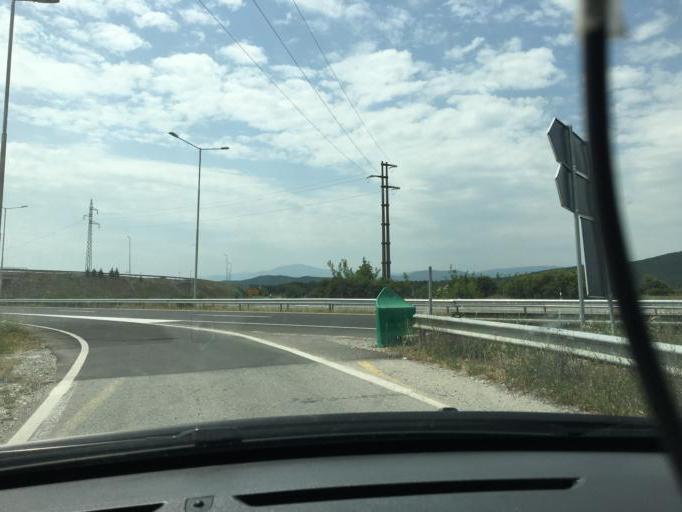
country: MK
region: Gevgelija
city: Gevgelija
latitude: 41.2050
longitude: 22.4961
